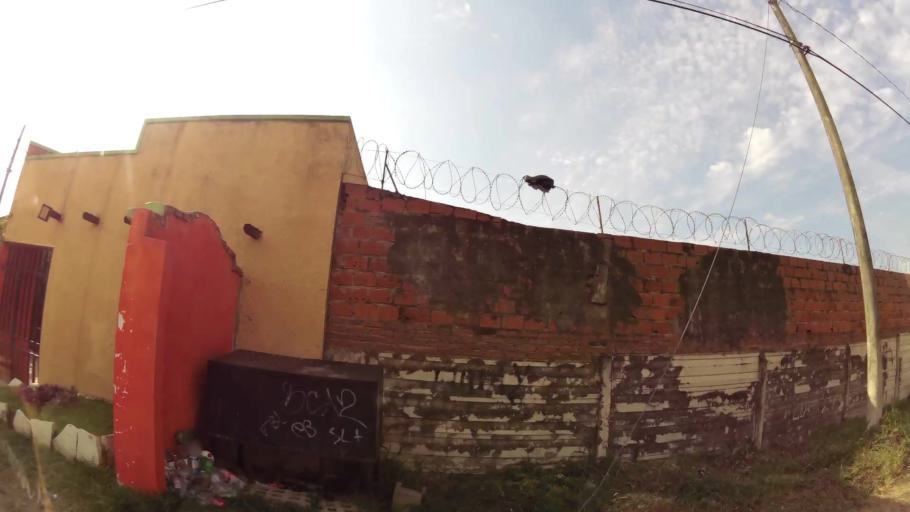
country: BO
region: Santa Cruz
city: Santa Cruz de la Sierra
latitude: -17.7244
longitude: -63.1740
